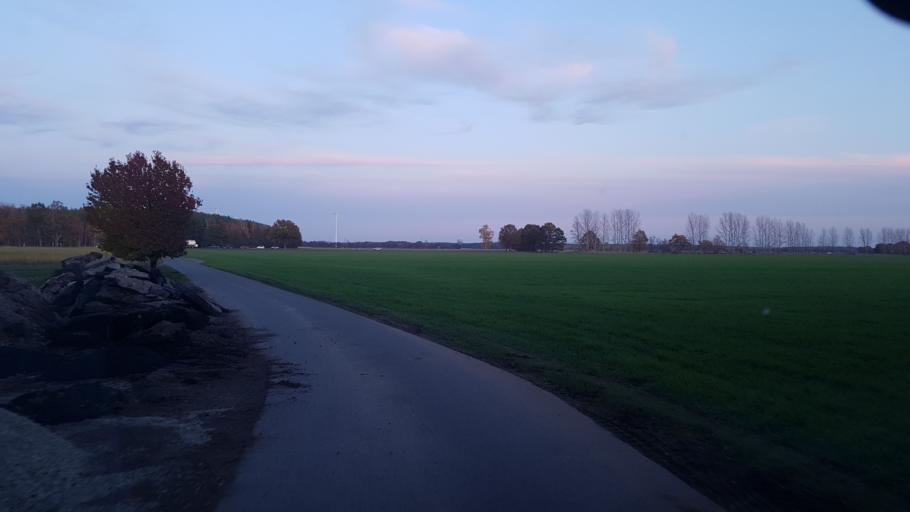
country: DE
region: Brandenburg
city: Schilda
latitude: 51.6216
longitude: 13.3216
